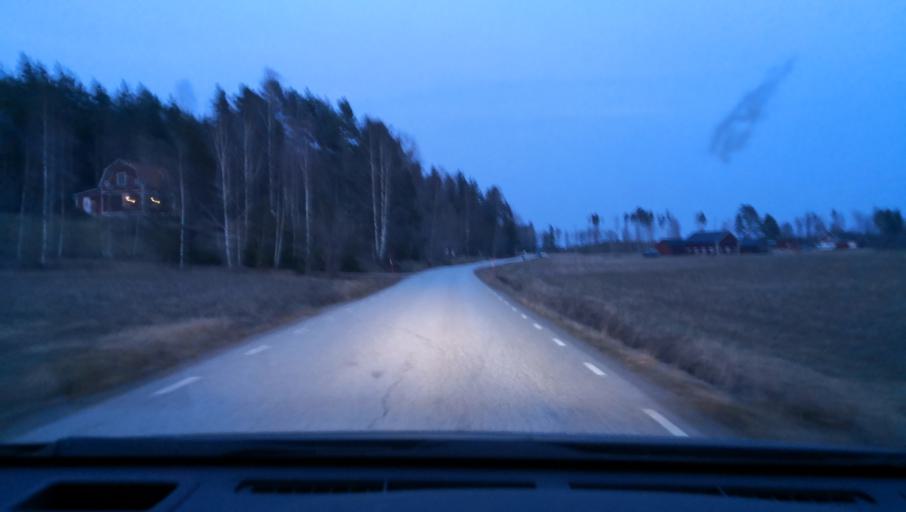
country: SE
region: OErebro
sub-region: Lindesbergs Kommun
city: Frovi
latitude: 59.5826
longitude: 15.4596
